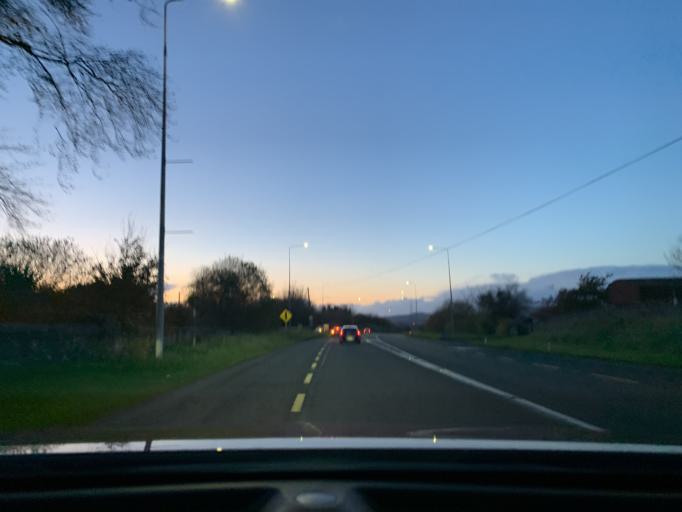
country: IE
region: Connaught
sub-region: Roscommon
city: Boyle
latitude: 53.9693
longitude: -8.2606
